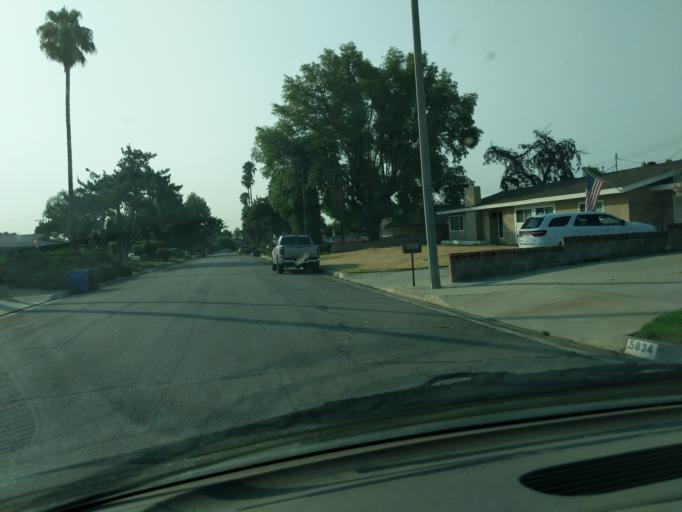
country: US
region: California
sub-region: San Bernardino County
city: Muscoy
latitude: 34.1476
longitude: -117.3834
